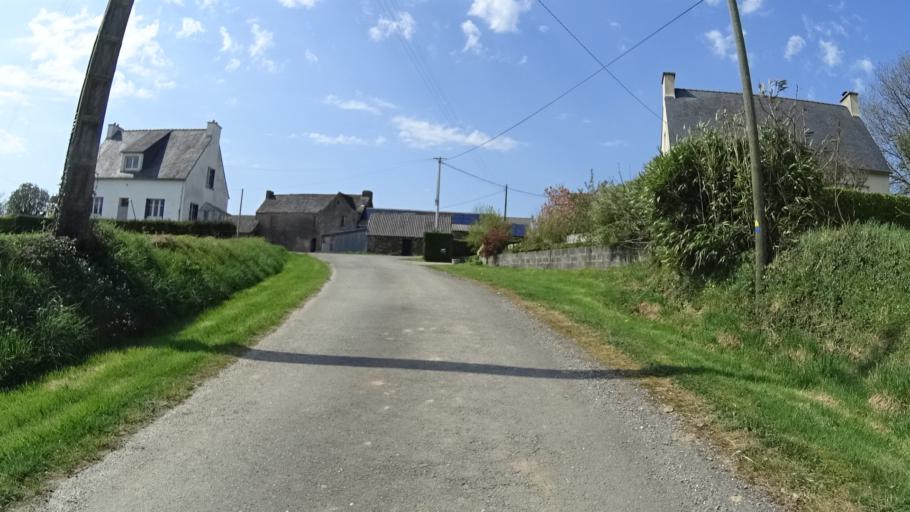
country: FR
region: Brittany
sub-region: Departement du Finistere
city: Sizun
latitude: 48.4180
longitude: -4.0922
